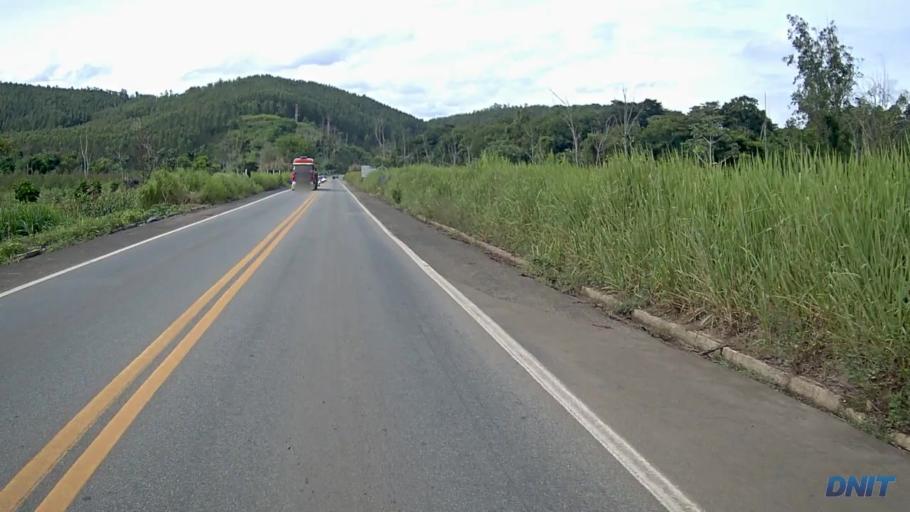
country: BR
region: Minas Gerais
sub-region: Ipaba
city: Ipaba
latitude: -19.3659
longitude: -42.4496
